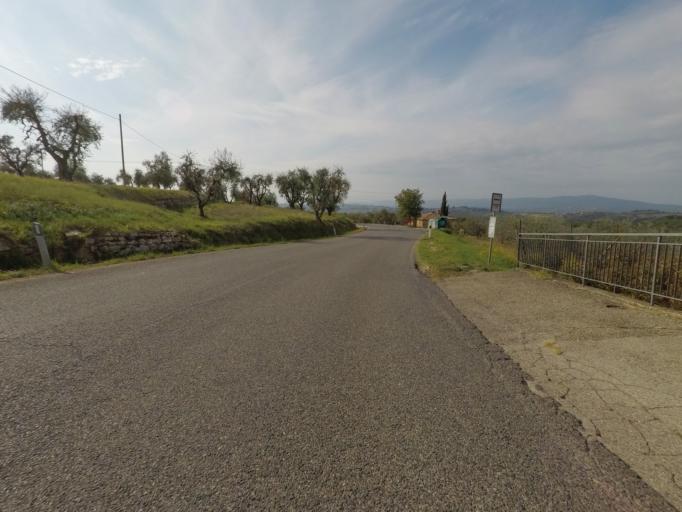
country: IT
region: Tuscany
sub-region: Provincia di Siena
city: Belverde
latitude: 43.3920
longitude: 11.3459
